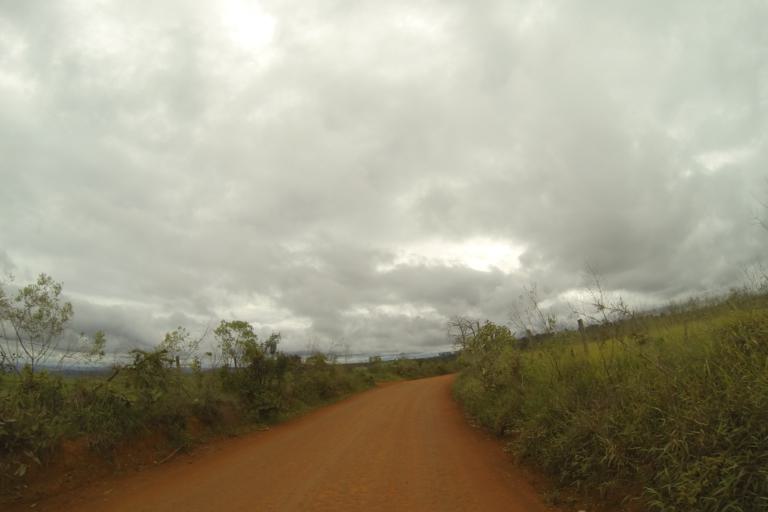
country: BR
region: Minas Gerais
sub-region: Campos Altos
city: Campos Altos
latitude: -19.8778
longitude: -46.3016
